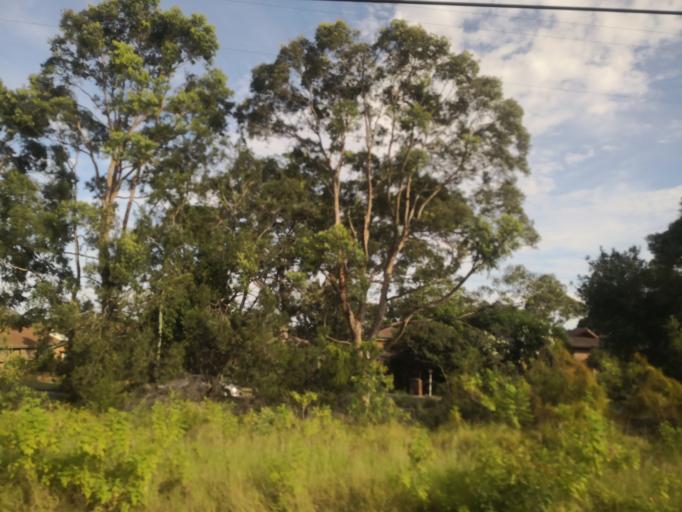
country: AU
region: New South Wales
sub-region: Gosford Shire
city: Blackwall
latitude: -33.4962
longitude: 151.3093
